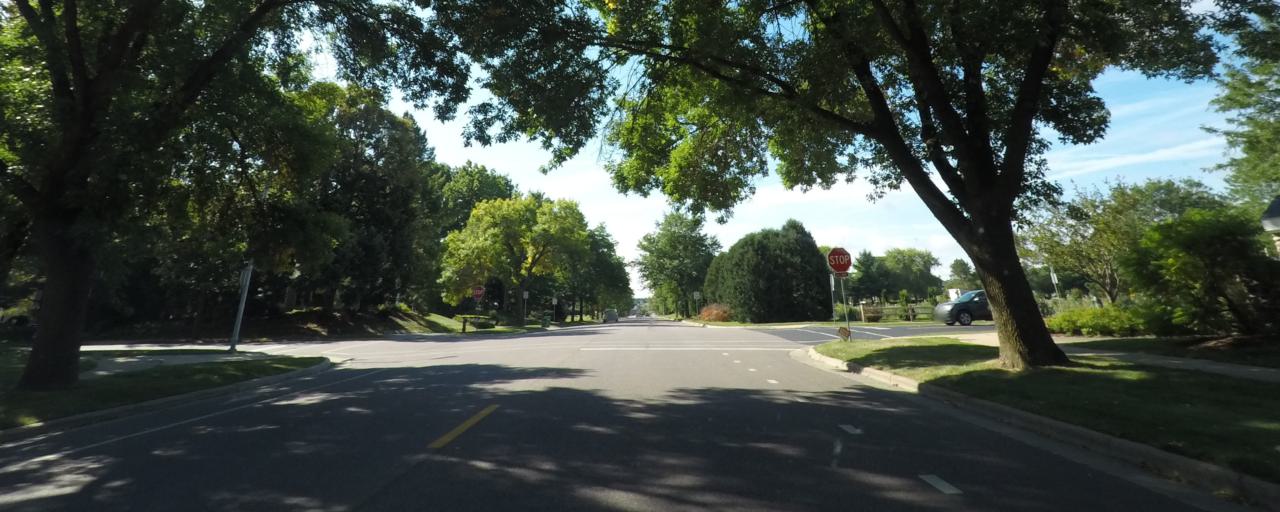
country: US
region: Wisconsin
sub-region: Dane County
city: Middleton
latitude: 43.0643
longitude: -89.5078
